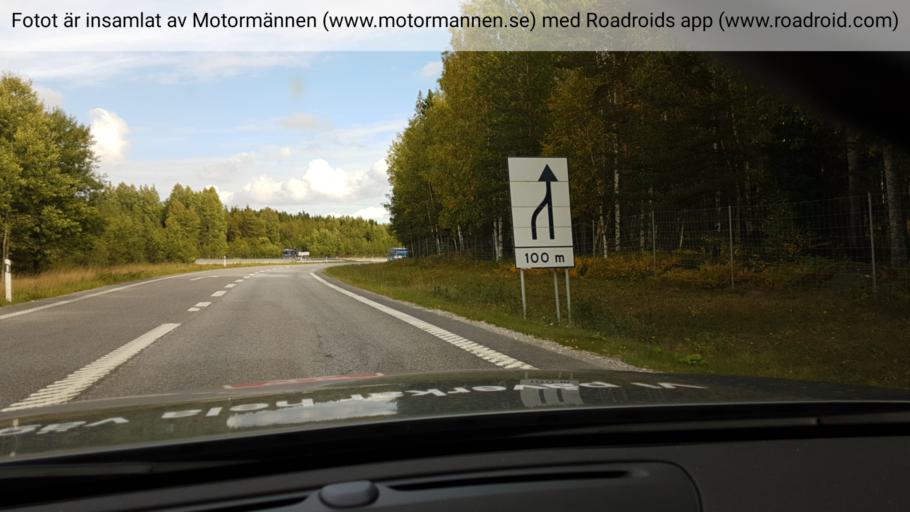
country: SE
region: Stockholm
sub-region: Norrtalje Kommun
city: Norrtalje
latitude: 59.7327
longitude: 18.5711
